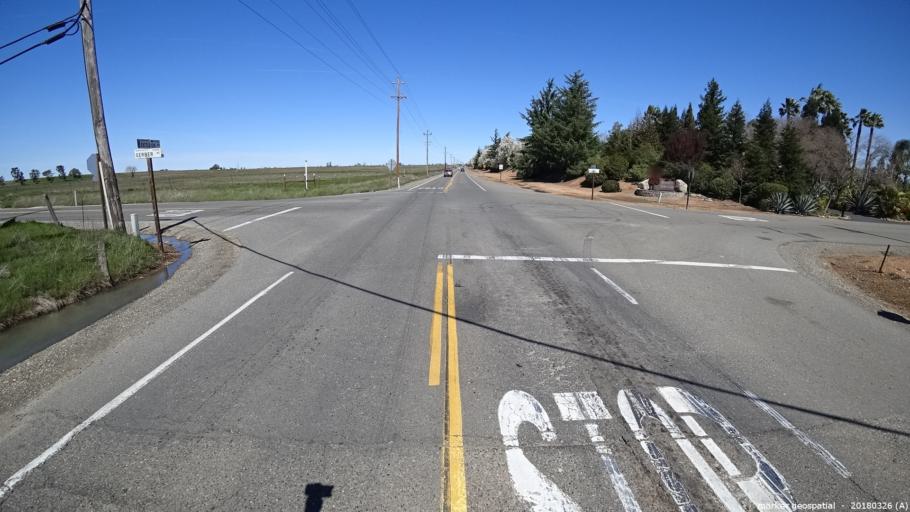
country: US
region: California
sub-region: Sacramento County
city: Vineyard
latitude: 38.4815
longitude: -121.2977
